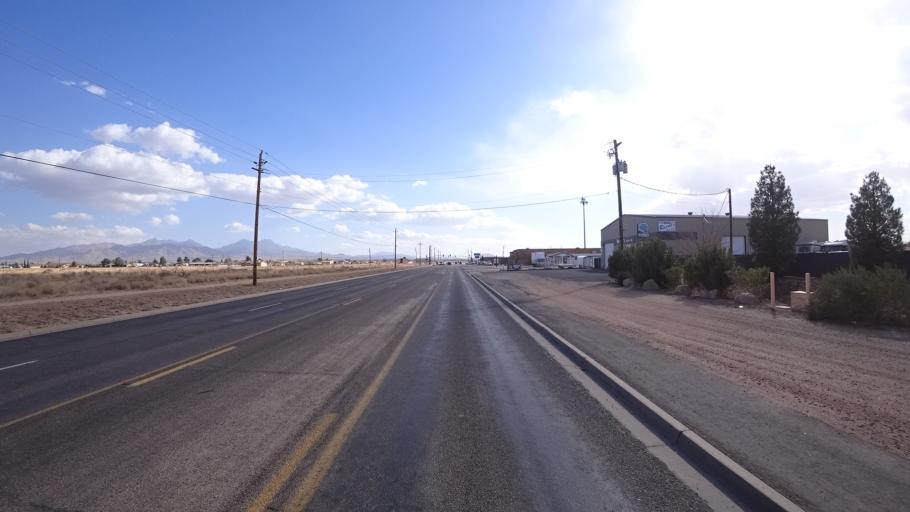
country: US
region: Arizona
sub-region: Mohave County
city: New Kingman-Butler
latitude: 35.2416
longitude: -114.0115
